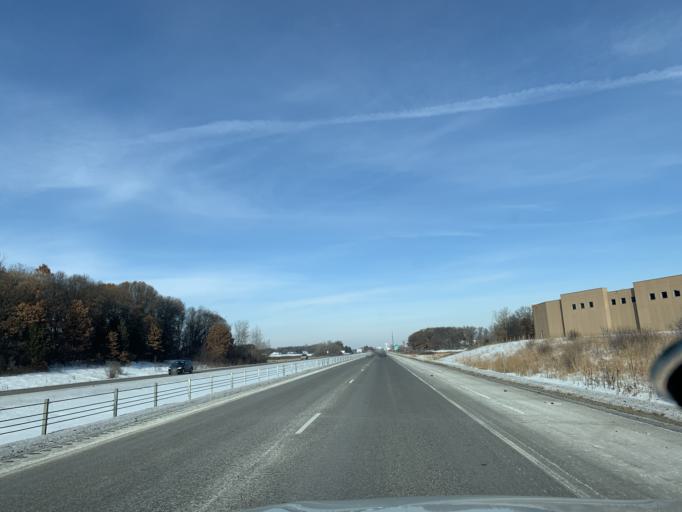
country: US
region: Minnesota
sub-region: Chisago County
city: Wyoming
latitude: 45.3160
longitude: -93.0033
